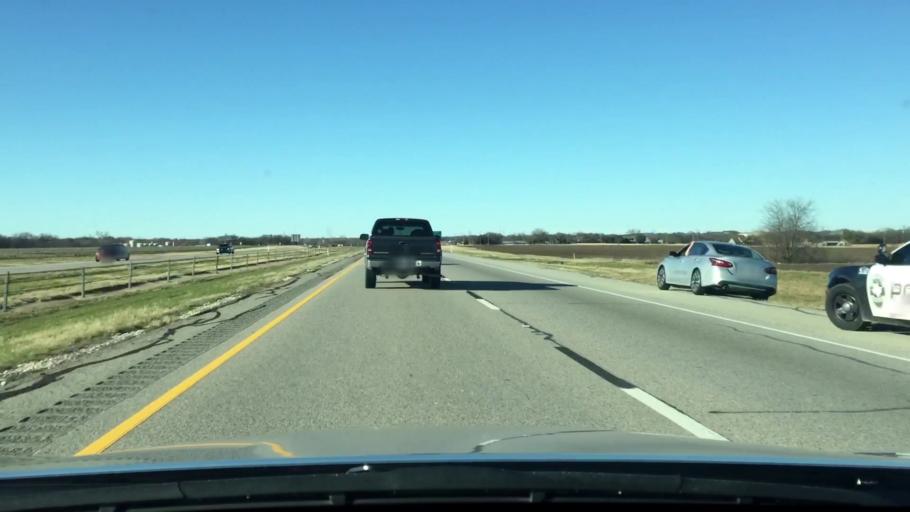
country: US
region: Texas
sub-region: Johnson County
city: Grandview
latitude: 32.2804
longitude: -97.1743
